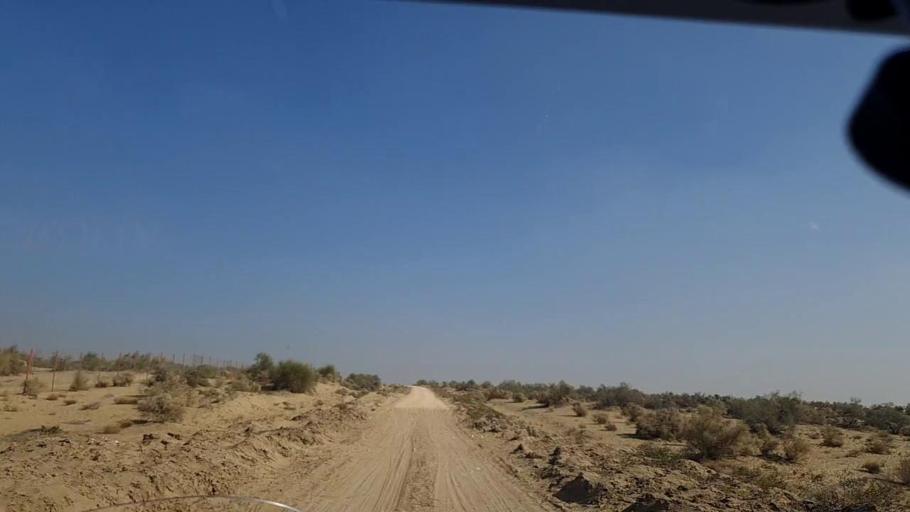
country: PK
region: Sindh
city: Khanpur
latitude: 27.5576
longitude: 69.3883
